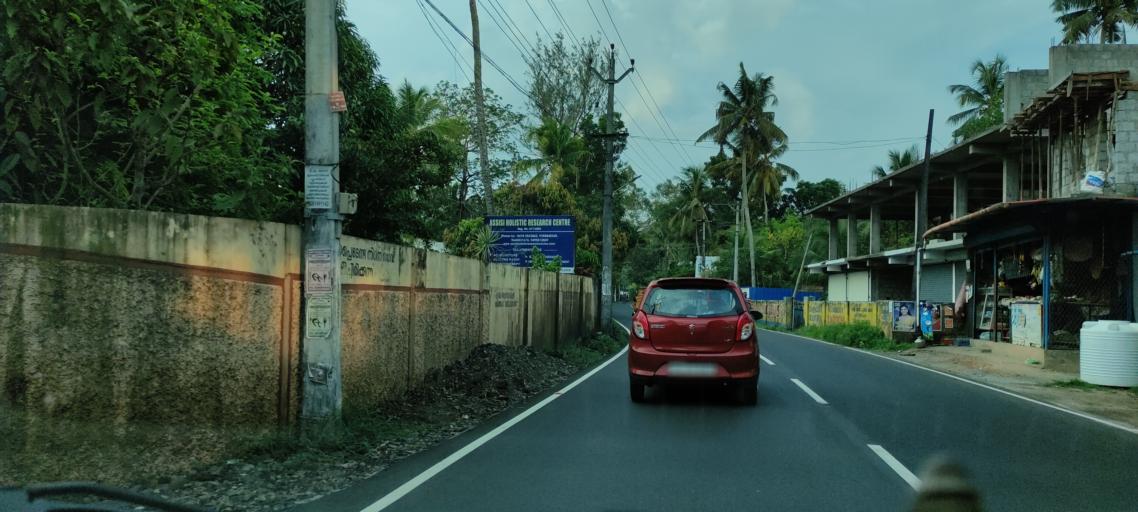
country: IN
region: Kerala
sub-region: Alappuzha
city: Kutiatodu
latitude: 9.8315
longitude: 76.3404
